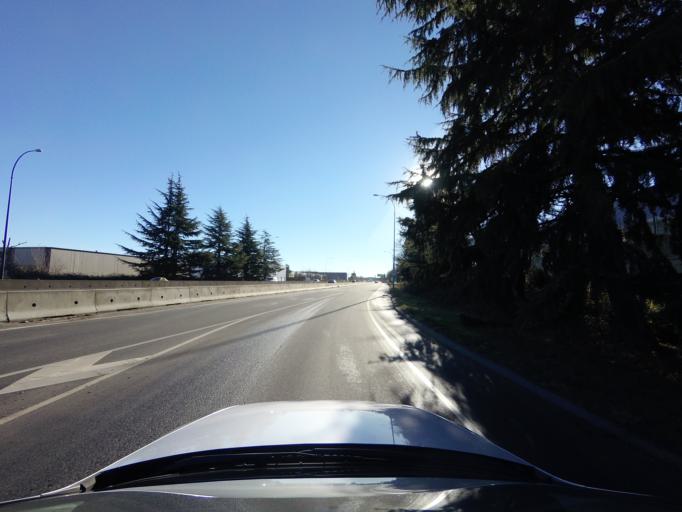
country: CA
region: British Columbia
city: Richmond
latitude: 49.1898
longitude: -123.0780
